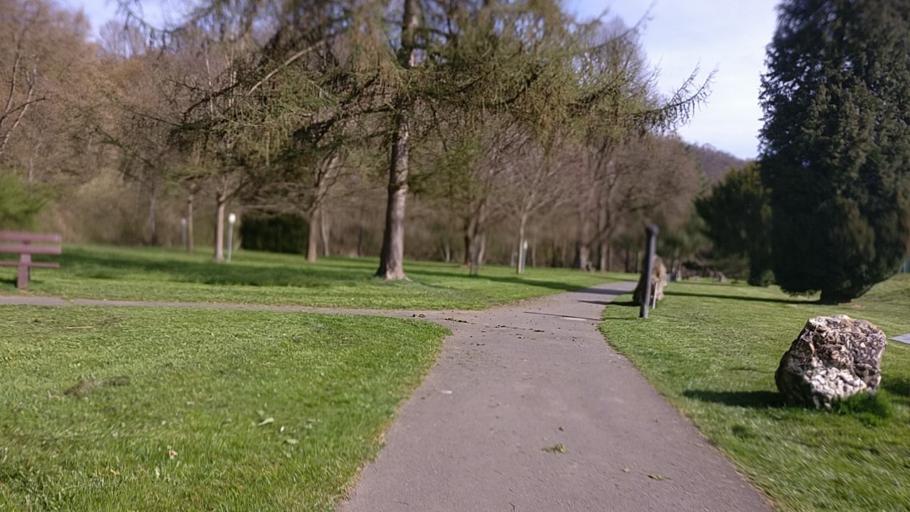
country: DE
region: Rheinland-Pfalz
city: Rossbach
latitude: 50.6224
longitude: 7.4238
